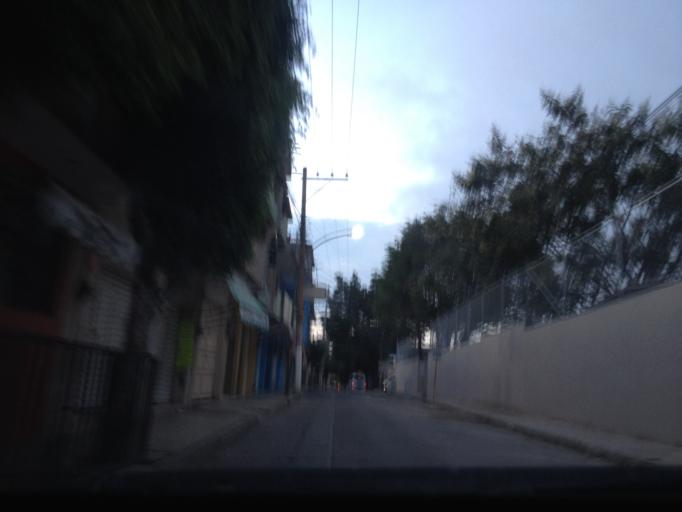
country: MX
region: Guerrero
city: Chilpancingo de los Bravos
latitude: 17.5579
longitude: -99.5042
